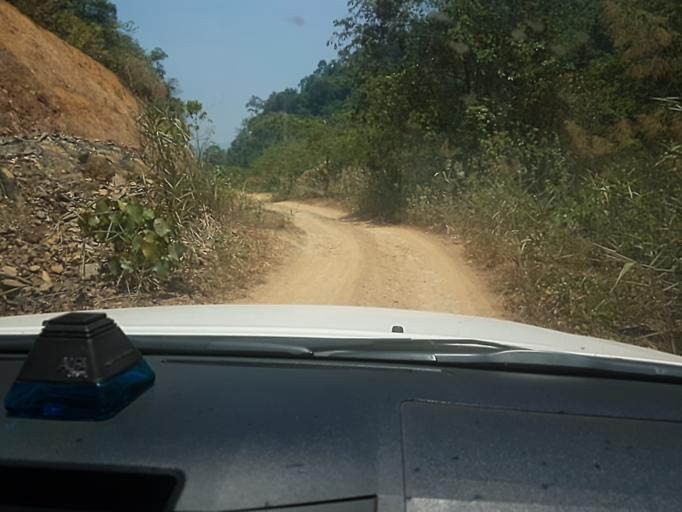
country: VN
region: Nghe An
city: Con Cuong
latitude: 18.6050
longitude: 104.7331
